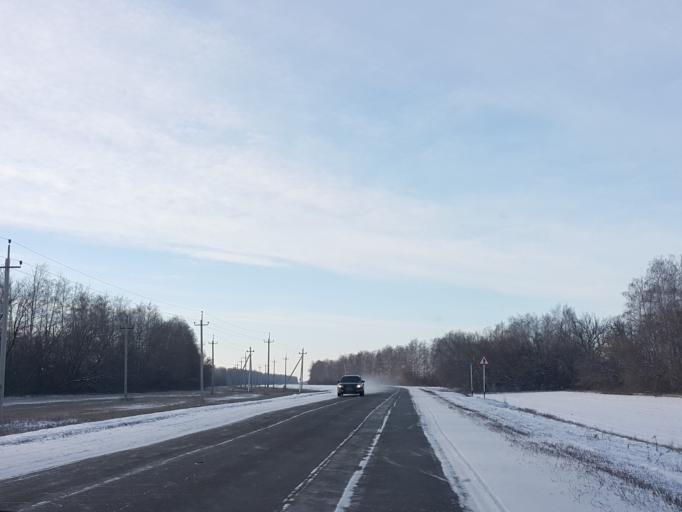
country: RU
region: Tambov
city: Znamenka
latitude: 52.3996
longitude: 41.3782
